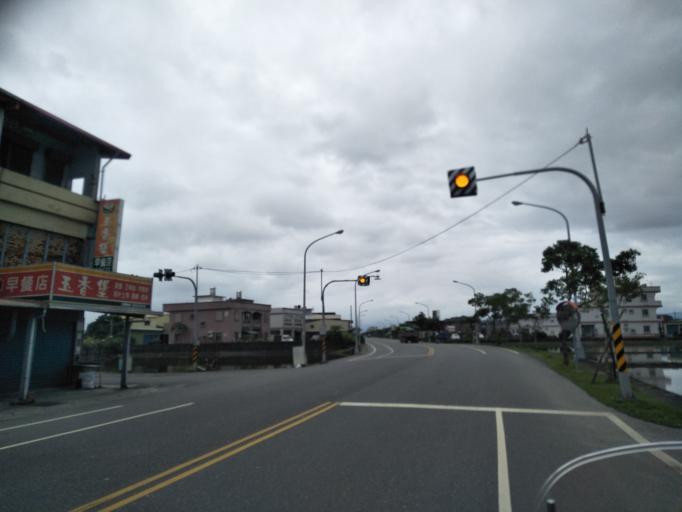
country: TW
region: Taiwan
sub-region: Yilan
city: Yilan
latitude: 24.7931
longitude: 121.7847
